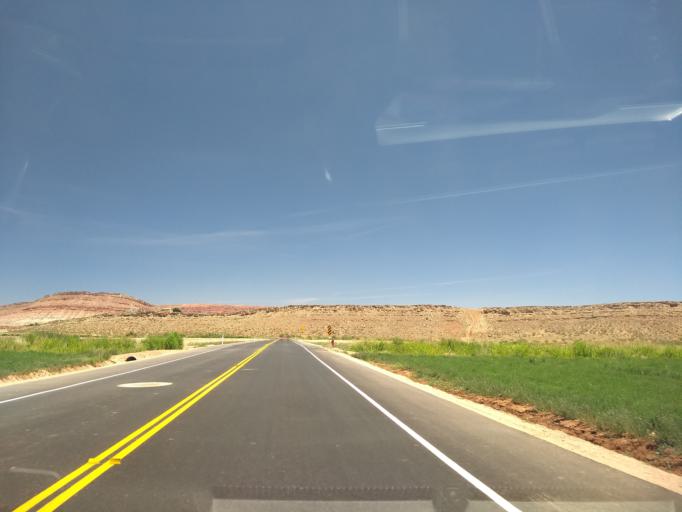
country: US
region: Utah
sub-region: Washington County
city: Washington
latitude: 37.0669
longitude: -113.5092
